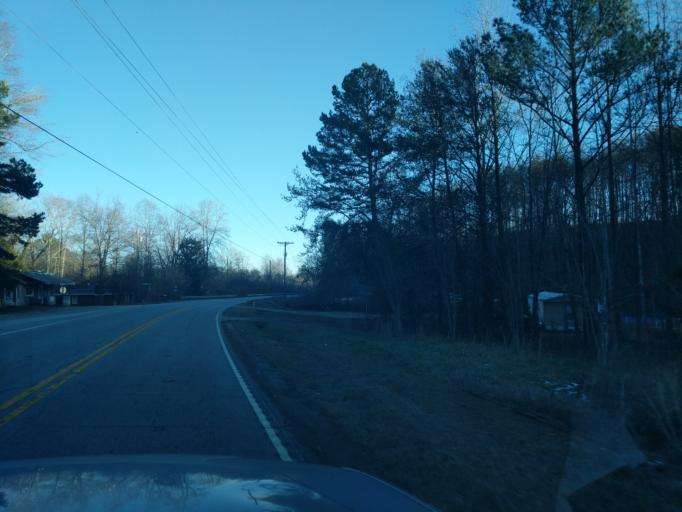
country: US
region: South Carolina
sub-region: Oconee County
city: Westminster
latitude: 34.7229
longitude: -83.2141
